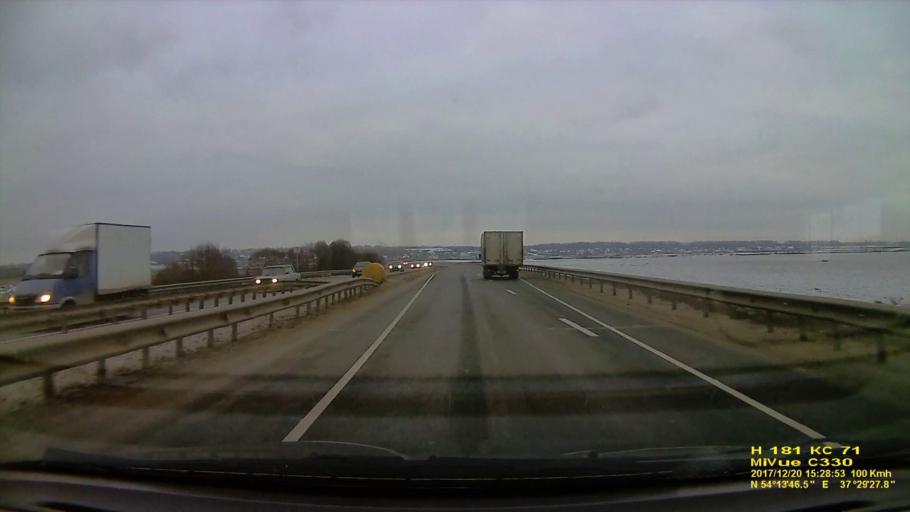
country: RU
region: Tula
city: Barsuki
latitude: 54.2295
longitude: 37.4909
